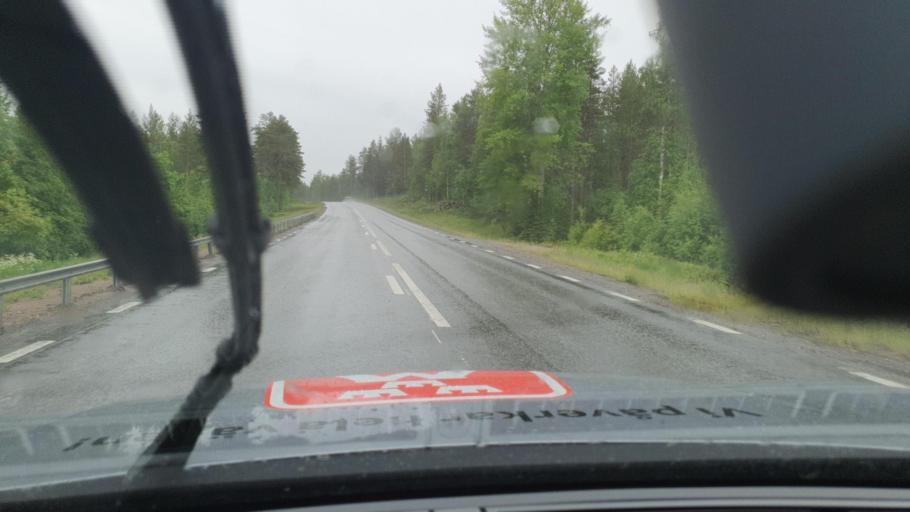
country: SE
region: Norrbotten
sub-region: Overkalix Kommun
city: OEverkalix
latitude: 66.2283
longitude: 22.7989
